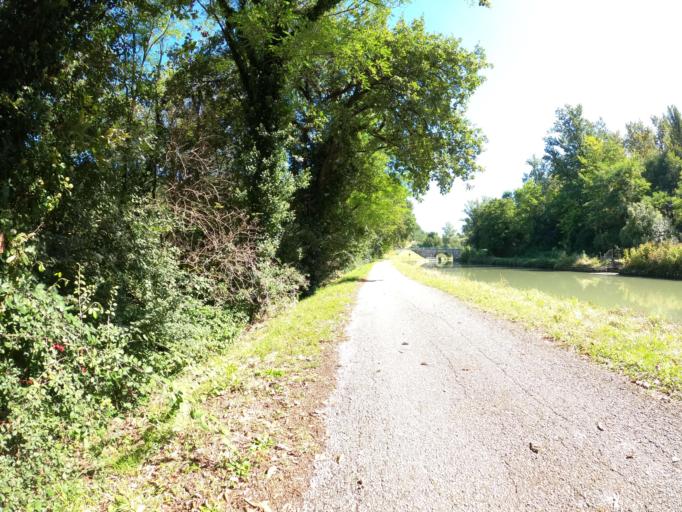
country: FR
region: Midi-Pyrenees
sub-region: Departement du Tarn-et-Garonne
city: Lamagistere
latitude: 44.1456
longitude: 0.7941
